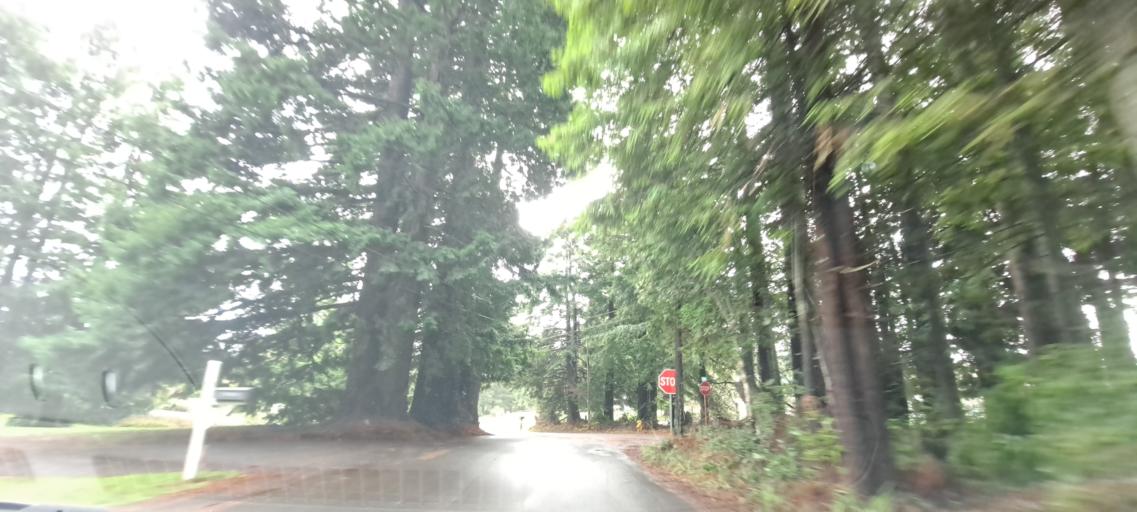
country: US
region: California
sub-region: Humboldt County
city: Fortuna
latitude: 40.6043
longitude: -124.1398
